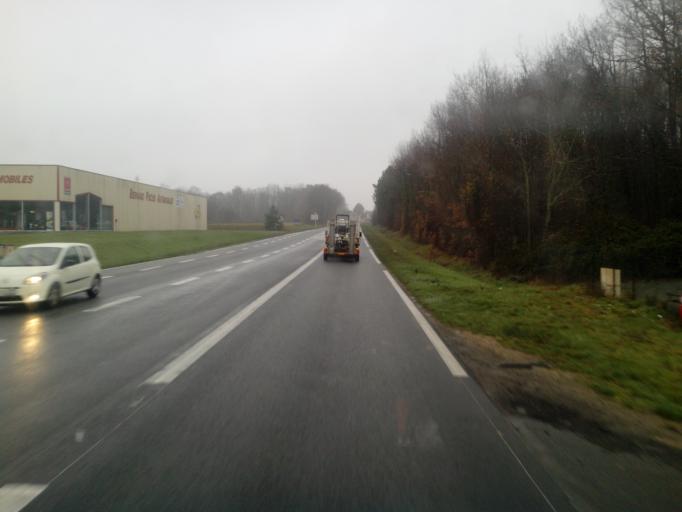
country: FR
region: Poitou-Charentes
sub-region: Departement de la Vienne
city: Mignaloux-Beauvoir
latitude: 46.5492
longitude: 0.4054
